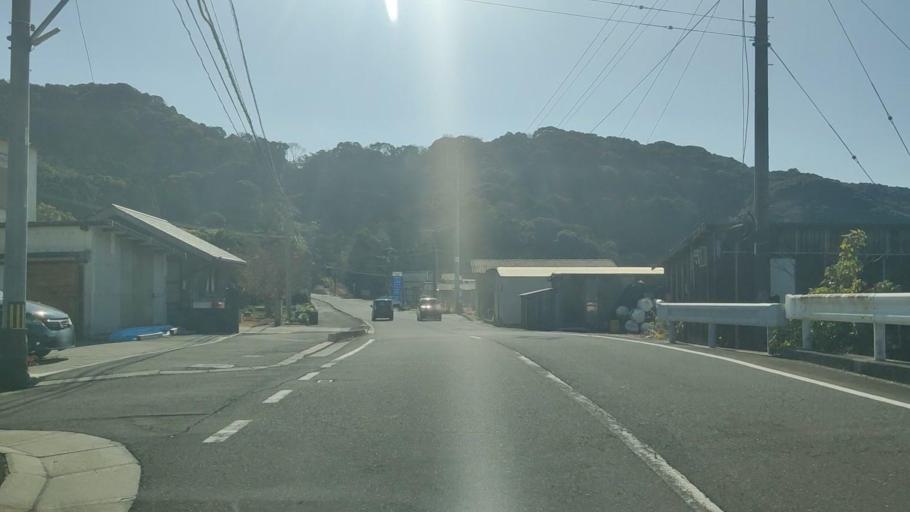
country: JP
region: Oita
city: Saiki
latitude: 32.8002
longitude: 131.9000
